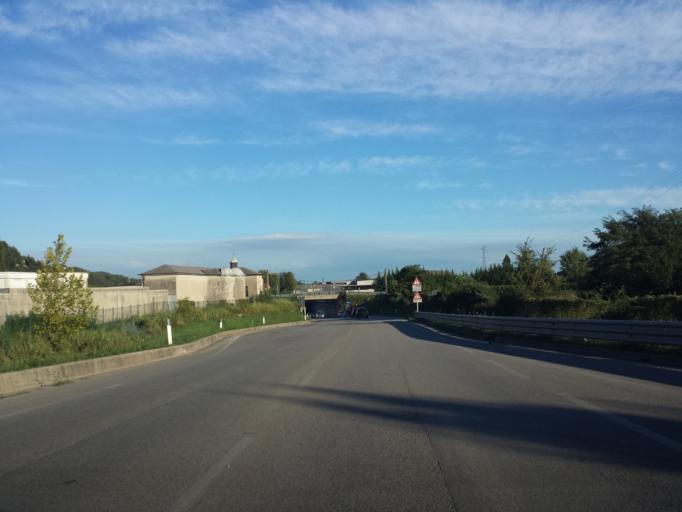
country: IT
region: Veneto
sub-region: Provincia di Vicenza
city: Cornedo Vicentino
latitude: 45.6119
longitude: 11.3355
